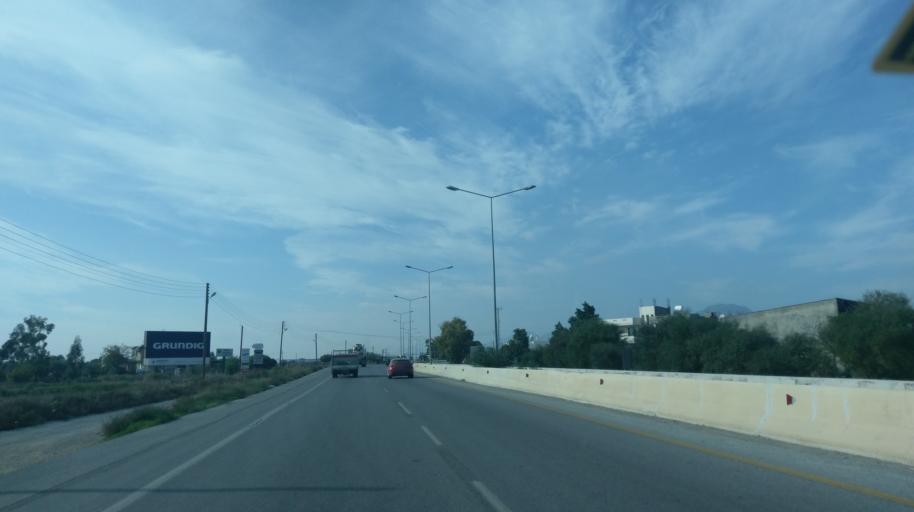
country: CY
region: Lefkosia
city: Geri
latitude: 35.2144
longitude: 33.5150
